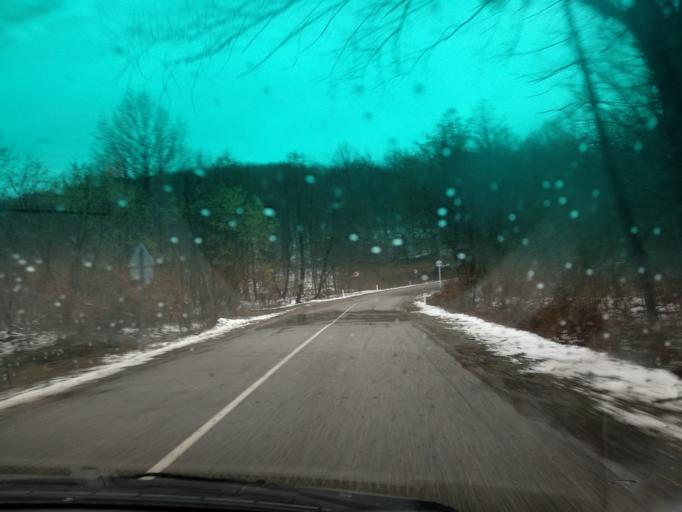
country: RU
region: Krasnodarskiy
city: Khadyzhensk
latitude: 44.2278
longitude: 39.3842
